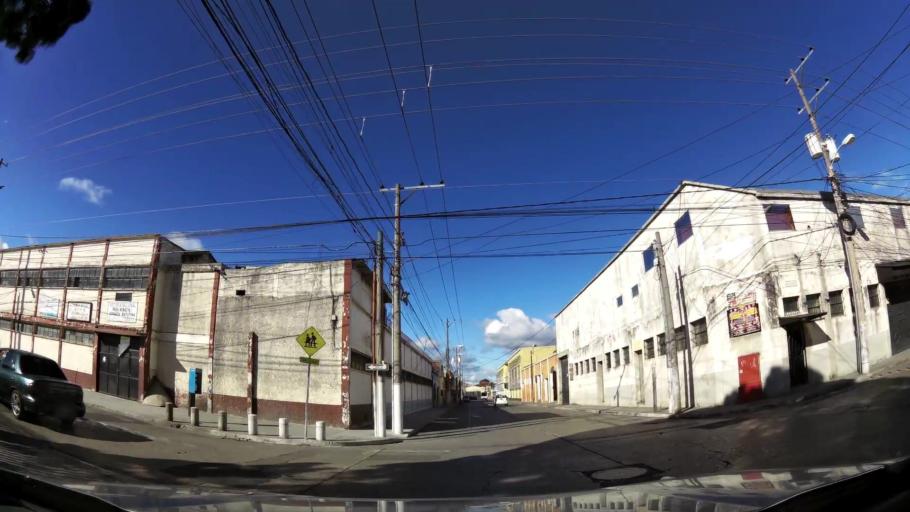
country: GT
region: Guatemala
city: Guatemala City
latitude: 14.6335
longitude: -90.5067
